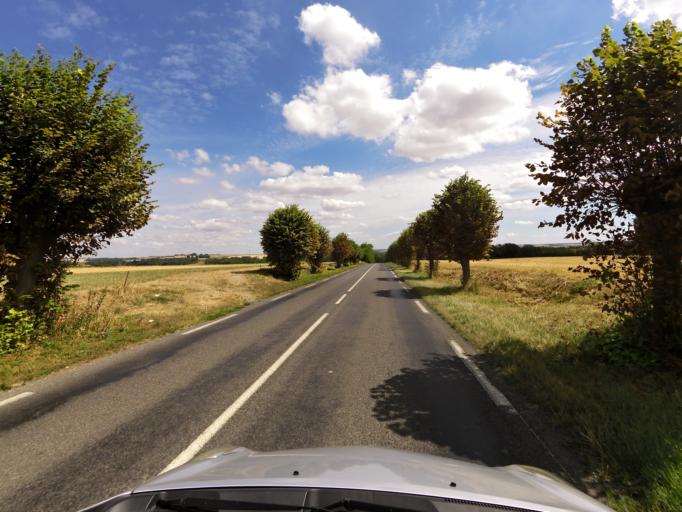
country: FR
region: Ile-de-France
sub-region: Departement de Seine-et-Marne
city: Varreddes
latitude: 49.0188
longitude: 2.9533
